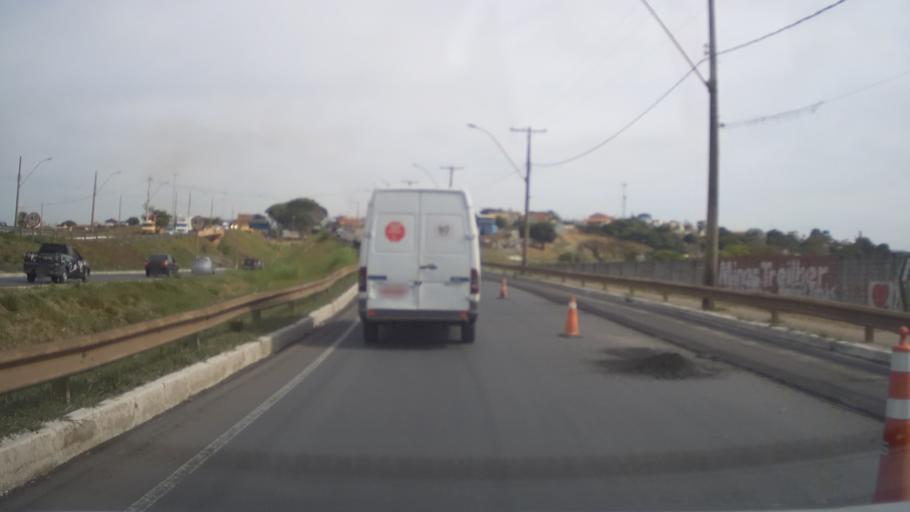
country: BR
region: Minas Gerais
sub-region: Contagem
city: Contagem
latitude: -19.9397
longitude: -44.0266
